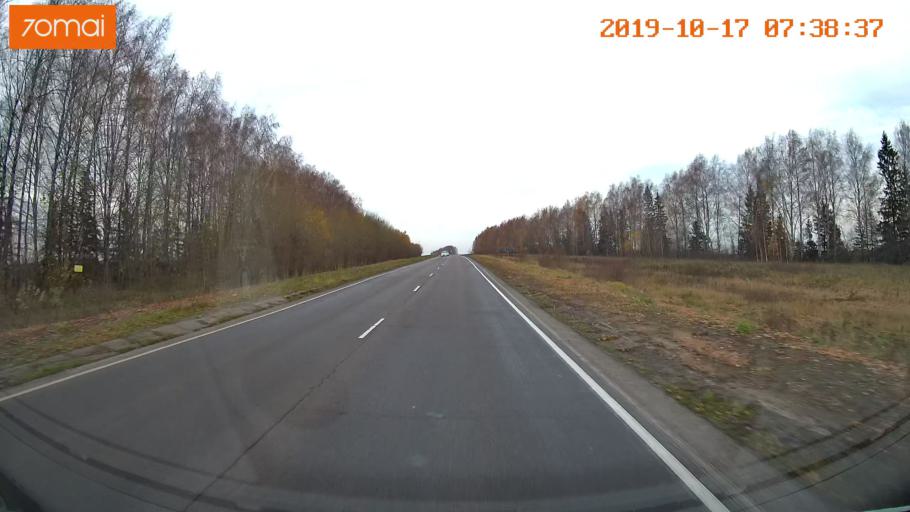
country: RU
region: Vladimir
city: Yur'yev-Pol'skiy
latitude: 56.4569
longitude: 39.8698
